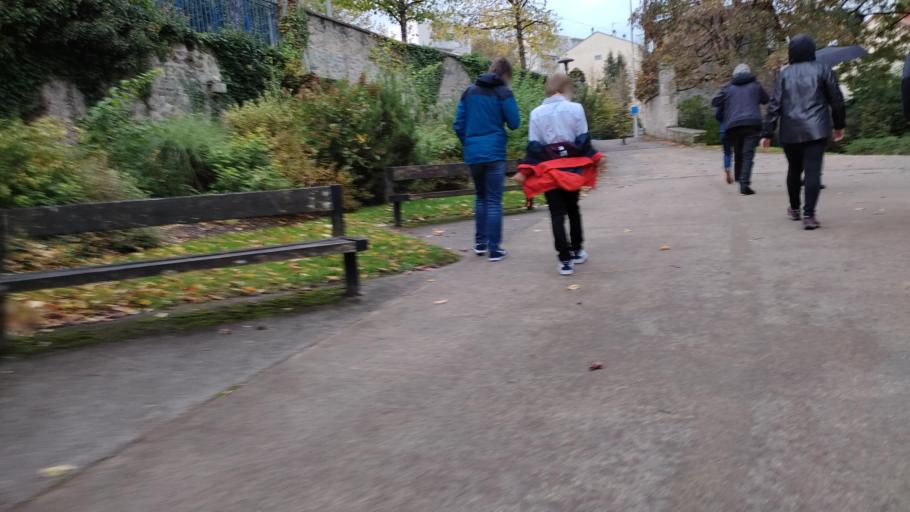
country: FR
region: Limousin
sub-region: Departement de la Haute-Vienne
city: Limoges
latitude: 45.8209
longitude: 1.2680
